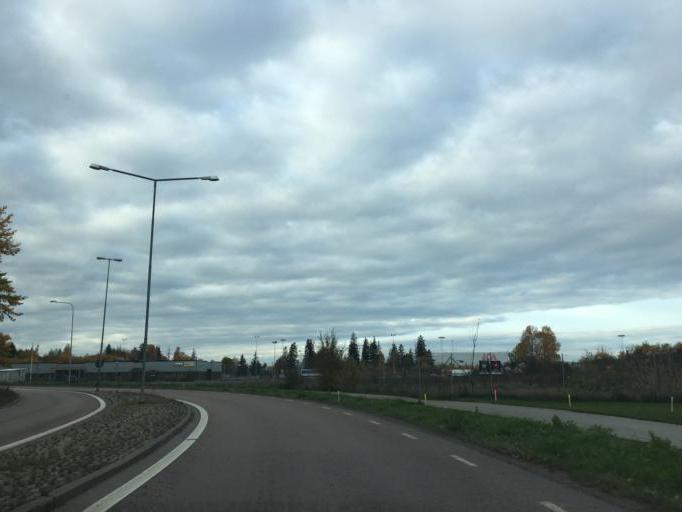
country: SE
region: Vaestmanland
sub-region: Vasteras
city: Vasteras
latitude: 59.5889
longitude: 16.4855
